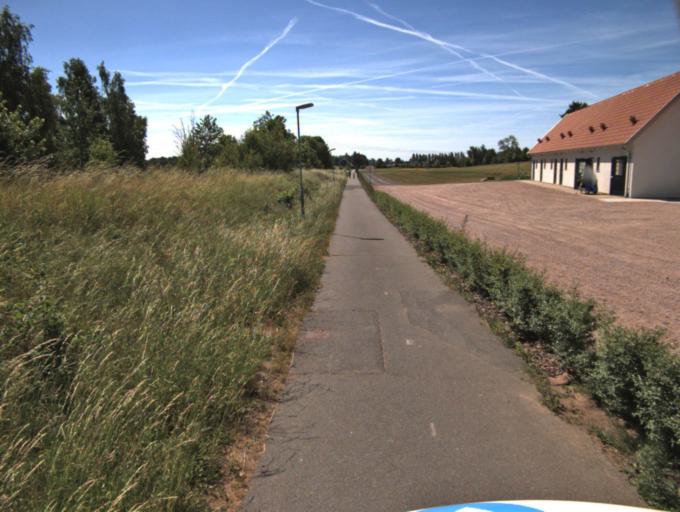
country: SE
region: Skane
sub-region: Kristianstads Kommun
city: Onnestad
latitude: 56.0669
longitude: 14.0881
